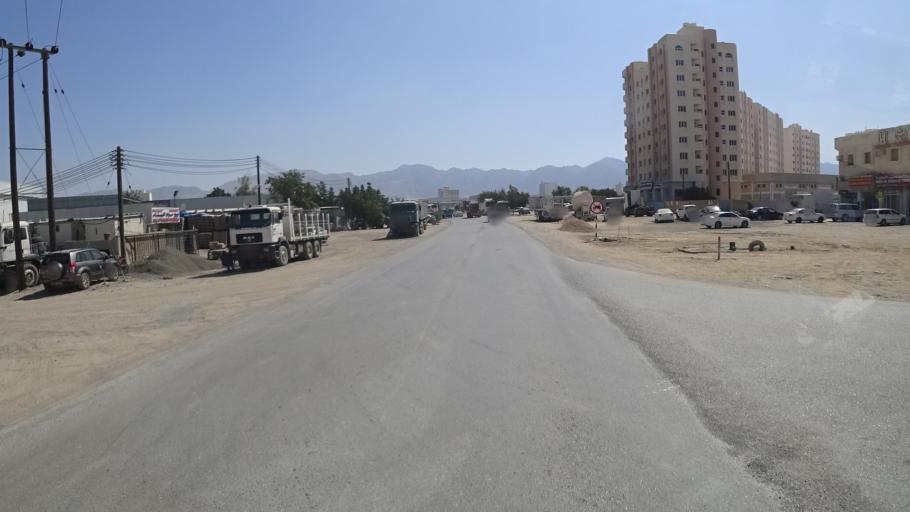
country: OM
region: Muhafazat Masqat
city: Bawshar
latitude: 23.5773
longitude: 58.3660
